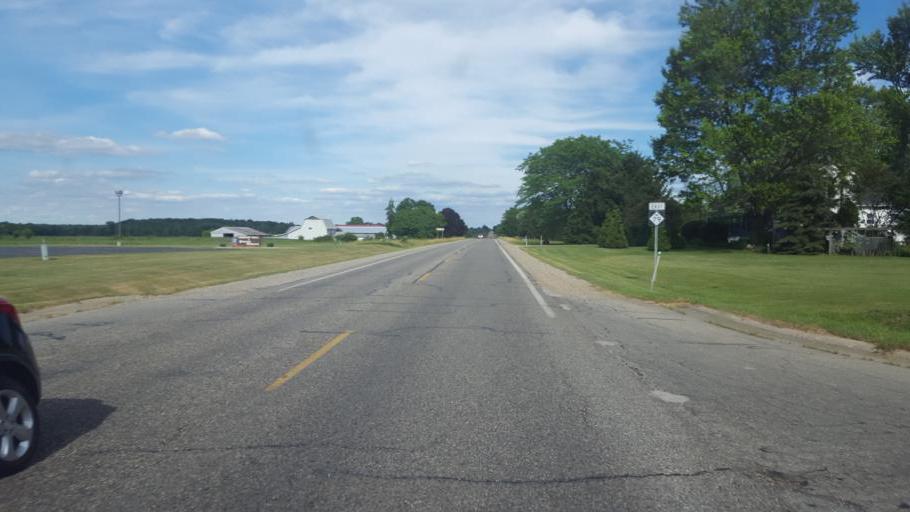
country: US
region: Michigan
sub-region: Eaton County
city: Charlotte
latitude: 42.5682
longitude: -84.9150
